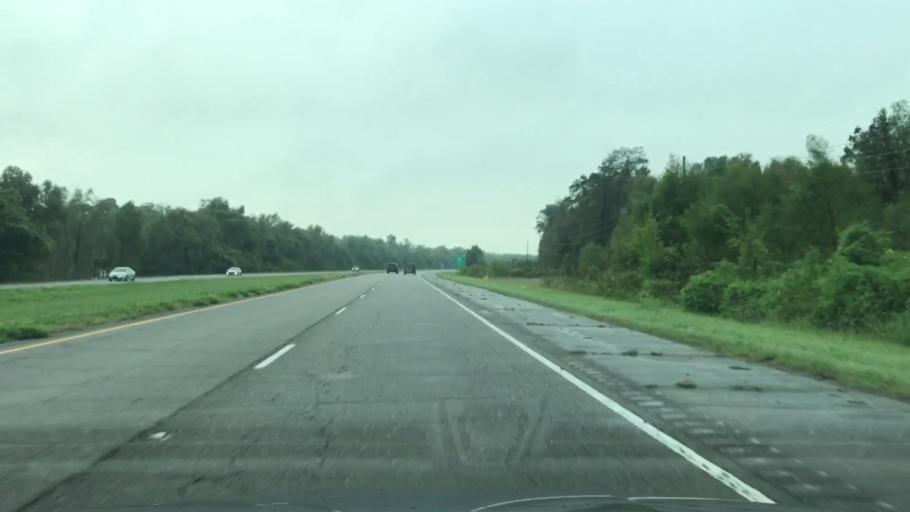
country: US
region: Louisiana
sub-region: Lafourche Parish
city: Raceland
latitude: 29.7263
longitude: -90.5593
